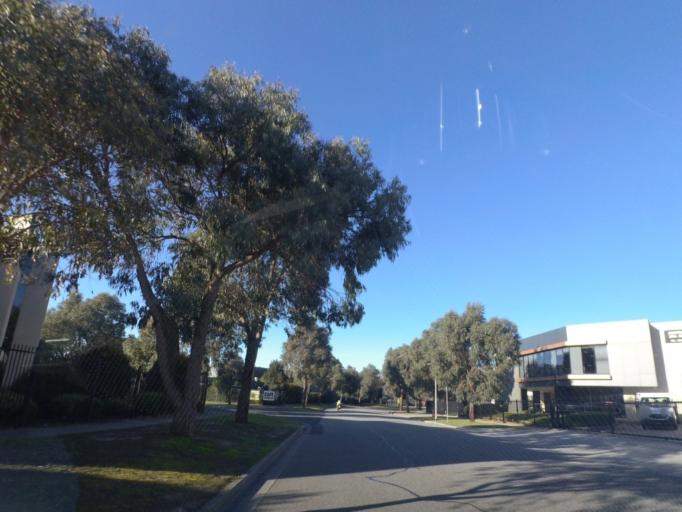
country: AU
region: Victoria
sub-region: Maroondah
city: Bayswater North
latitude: -37.8142
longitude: 145.2980
